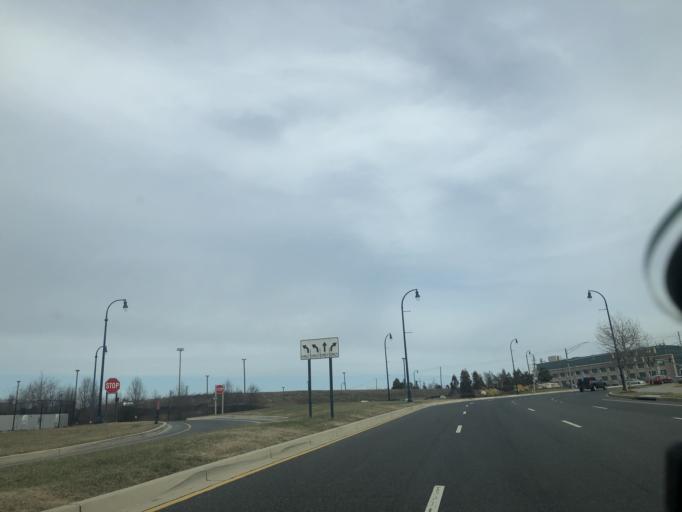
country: US
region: Maryland
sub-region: Prince George's County
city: Forest Heights
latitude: 38.7967
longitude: -77.0047
